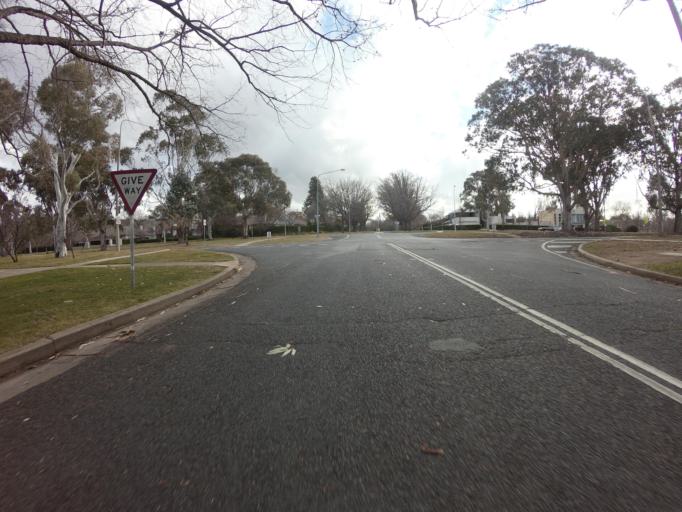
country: AU
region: Australian Capital Territory
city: Forrest
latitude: -35.3157
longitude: 149.1253
